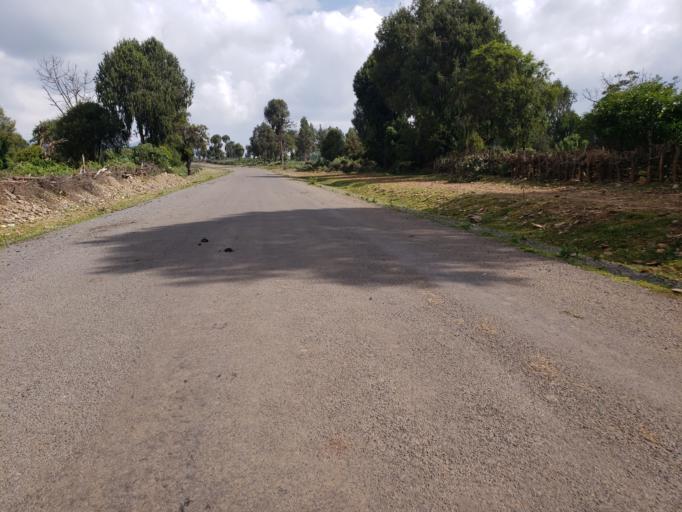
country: ET
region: Oromiya
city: Dodola
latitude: 6.8651
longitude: 39.3909
